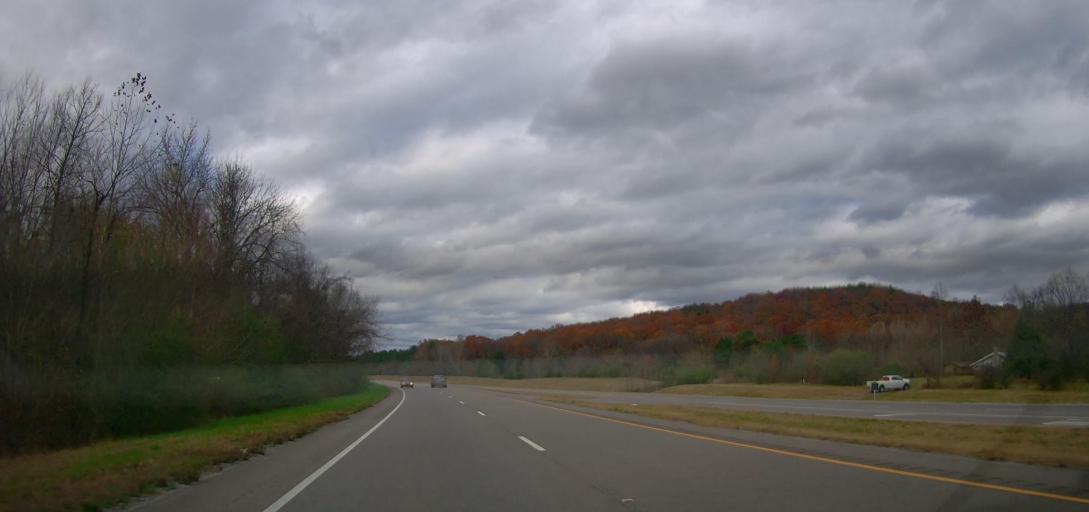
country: US
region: Alabama
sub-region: Morgan County
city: Falkville
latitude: 34.3239
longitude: -87.0017
